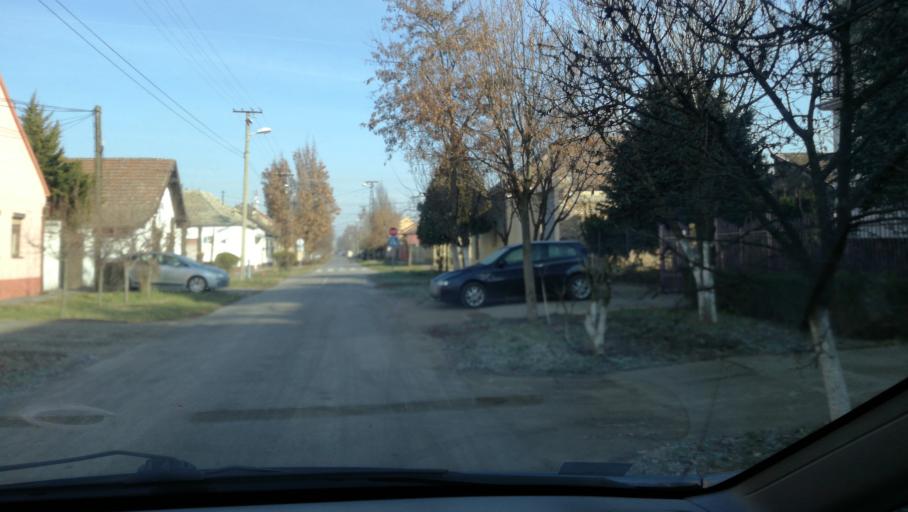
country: RS
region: Autonomna Pokrajina Vojvodina
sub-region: Severnobanatski Okrug
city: Kikinda
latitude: 45.8247
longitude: 20.4614
